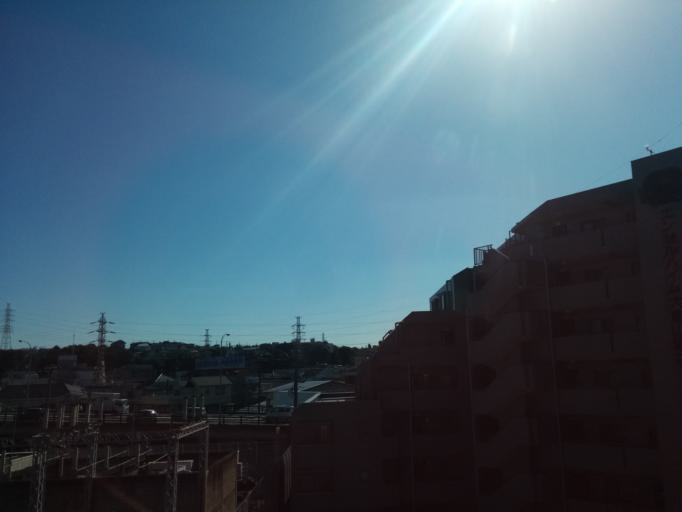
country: JP
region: Kanagawa
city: Yokohama
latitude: 35.5172
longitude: 139.6291
